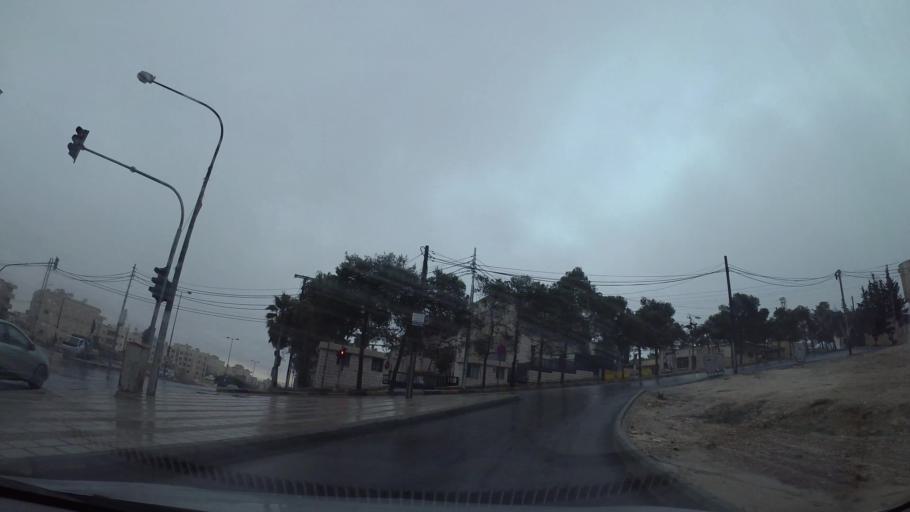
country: JO
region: Amman
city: Al Jubayhah
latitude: 32.0309
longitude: 35.8774
